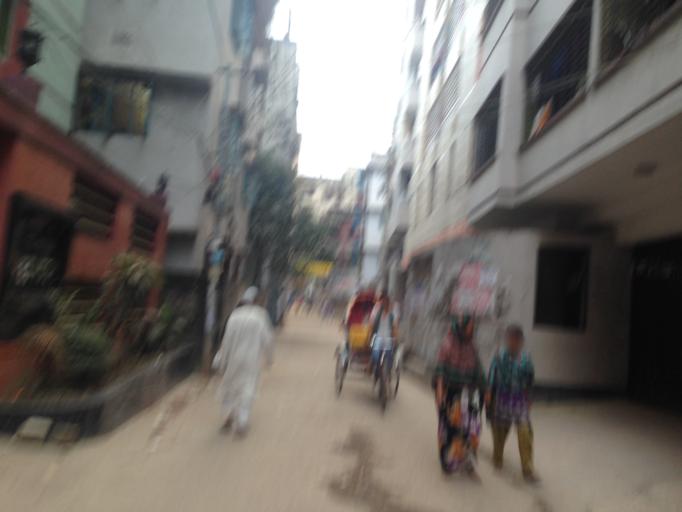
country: BD
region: Dhaka
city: Paltan
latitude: 23.7460
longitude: 90.4212
